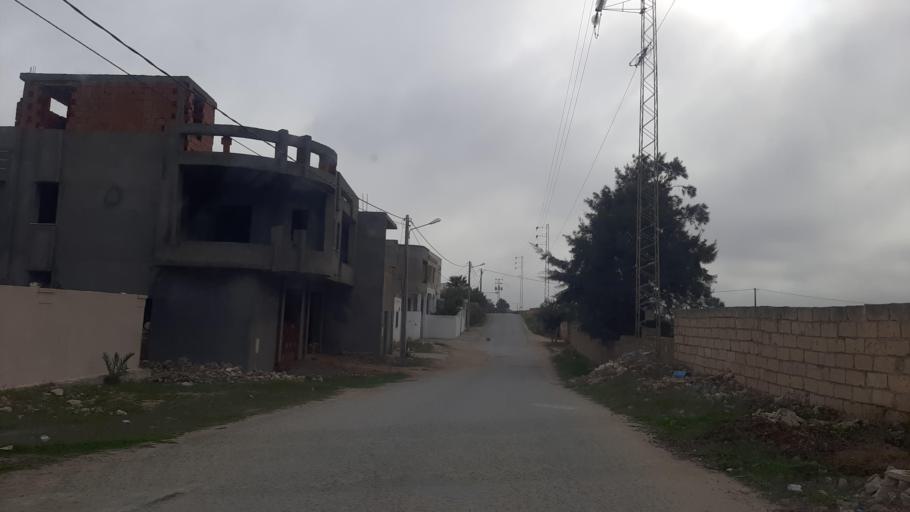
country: TN
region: Nabul
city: Menzel Heurr
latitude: 36.6784
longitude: 10.9239
